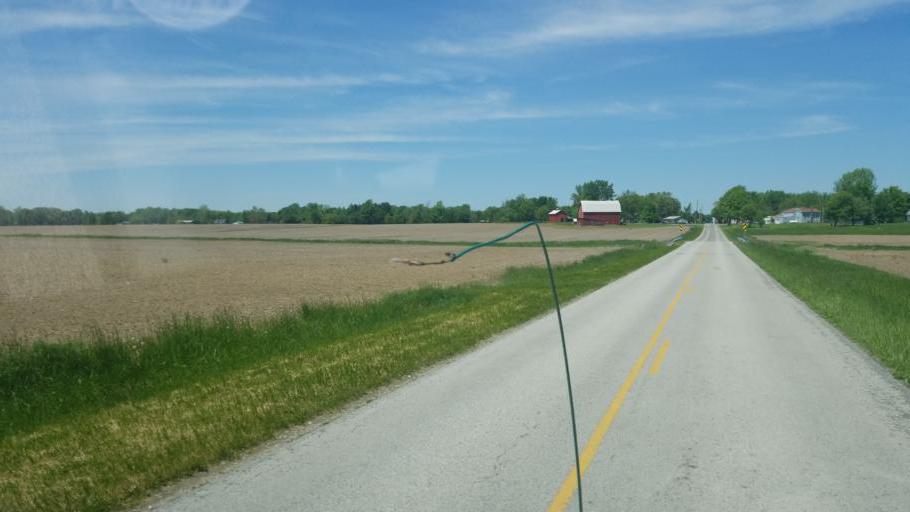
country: US
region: Ohio
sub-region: Huron County
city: Greenwich
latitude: 41.1485
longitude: -82.5385
